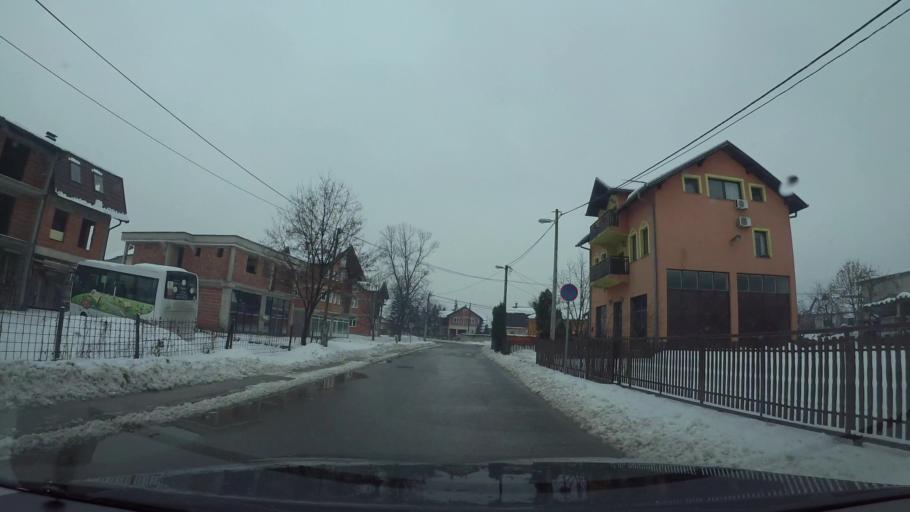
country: BA
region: Federation of Bosnia and Herzegovina
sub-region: Kanton Sarajevo
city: Sarajevo
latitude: 43.8490
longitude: 18.2798
